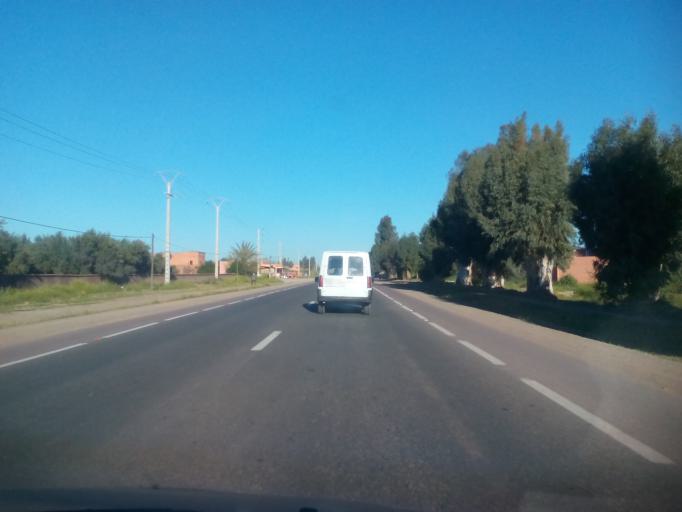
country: MA
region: Marrakech-Tensift-Al Haouz
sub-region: Marrakech
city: Marrakesh
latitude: 31.6320
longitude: -8.1970
